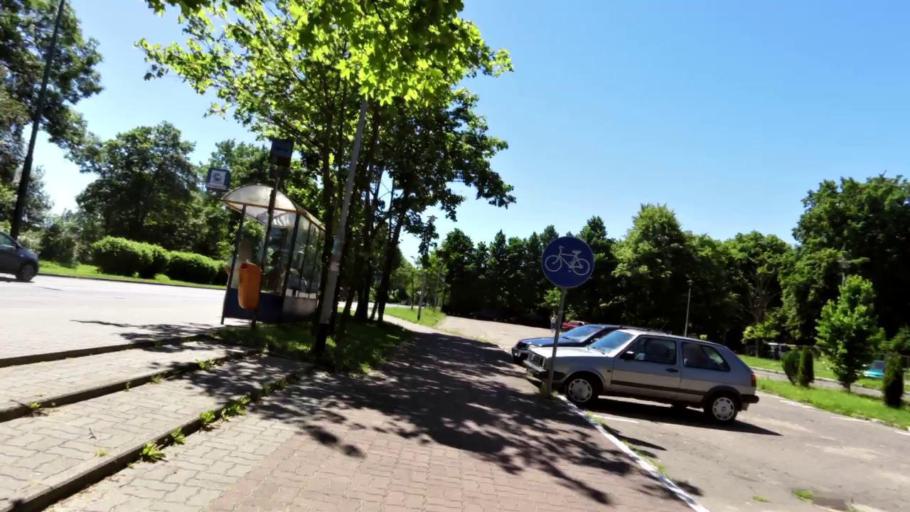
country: PL
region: West Pomeranian Voivodeship
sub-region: Powiat kolobrzeski
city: Kolobrzeg
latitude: 54.1580
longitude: 15.5653
